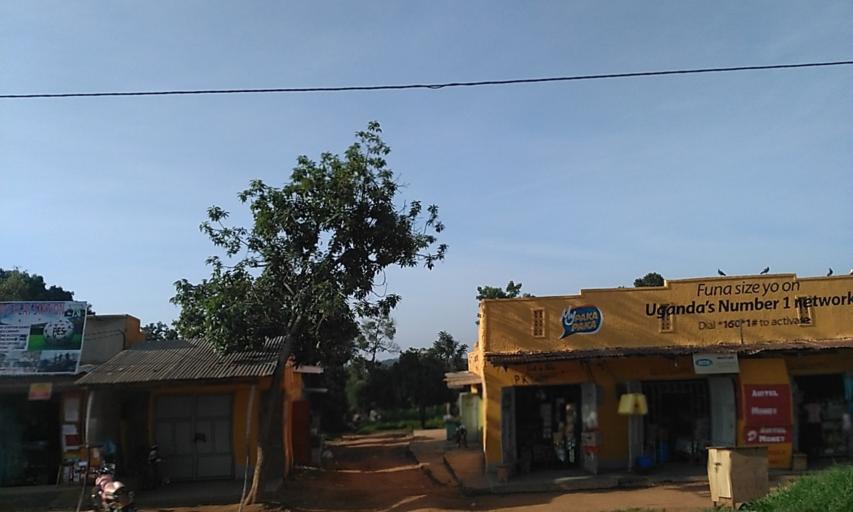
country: UG
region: Central Region
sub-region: Wakiso District
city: Bweyogerere
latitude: 0.4601
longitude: 32.6292
